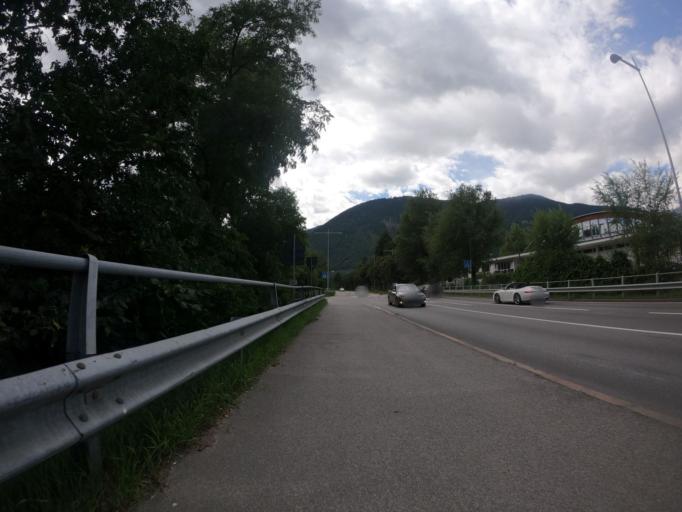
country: IT
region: Trentino-Alto Adige
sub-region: Bolzano
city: Sinigo
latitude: 46.6281
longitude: 11.1656
